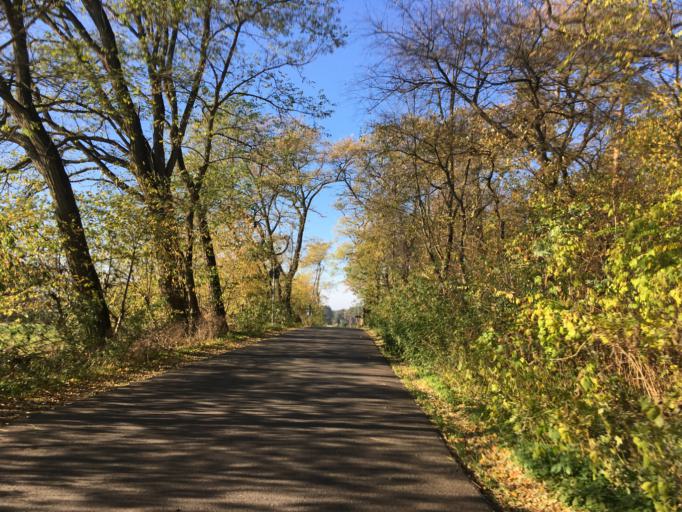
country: DE
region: Brandenburg
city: Reichenwalde
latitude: 52.2893
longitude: 14.0171
